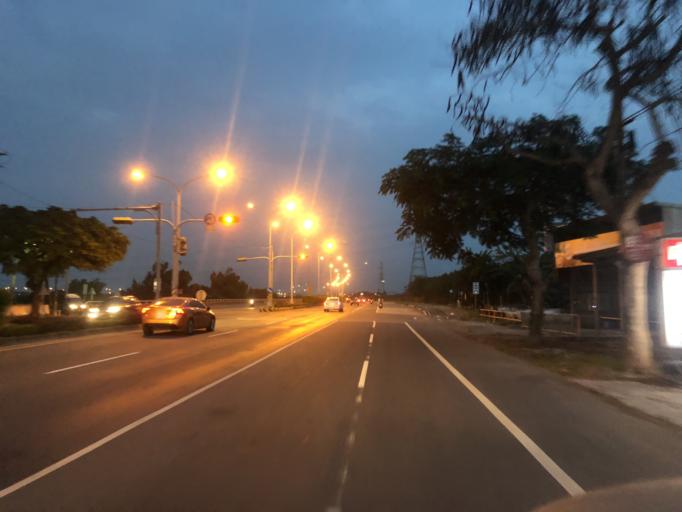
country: TW
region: Taiwan
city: Yujing
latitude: 23.1499
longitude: 120.3335
